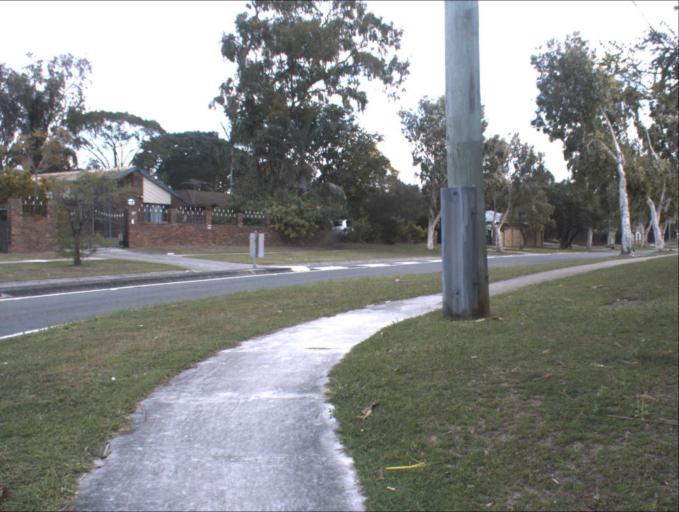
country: AU
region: Queensland
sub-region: Brisbane
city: Sunnybank Hills
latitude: -27.6679
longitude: 153.0438
